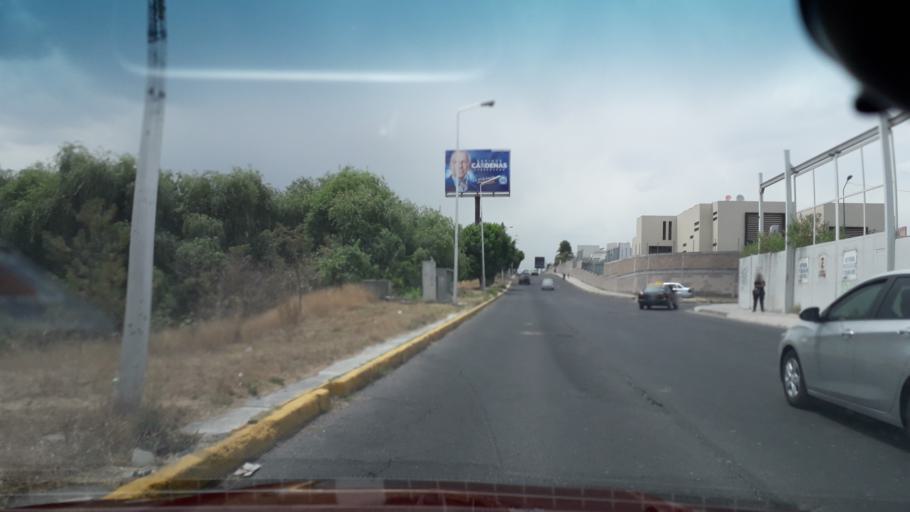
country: MX
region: Puebla
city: Puebla
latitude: 19.0202
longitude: -98.2369
